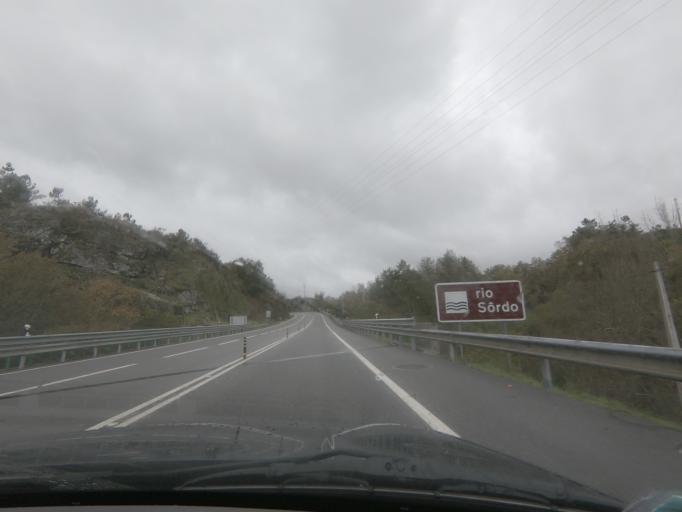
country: PT
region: Vila Real
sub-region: Santa Marta de Penaguiao
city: Santa Marta de Penaguiao
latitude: 41.2845
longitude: -7.8276
